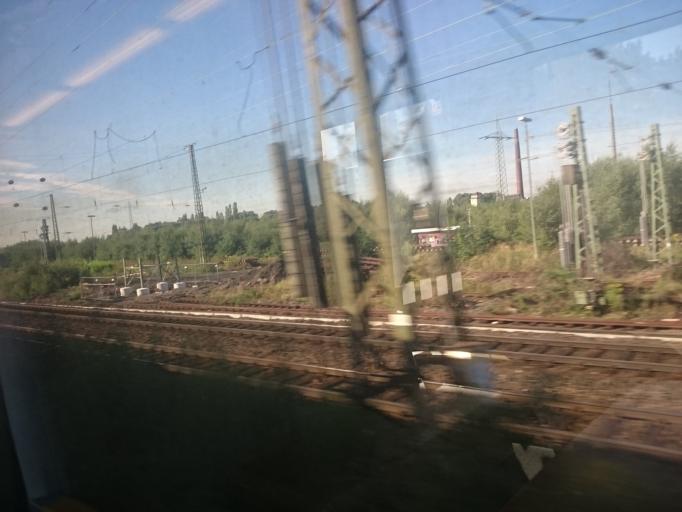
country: DE
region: North Rhine-Westphalia
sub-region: Regierungsbezirk Dusseldorf
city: Duisburg
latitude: 51.4031
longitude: 6.8015
